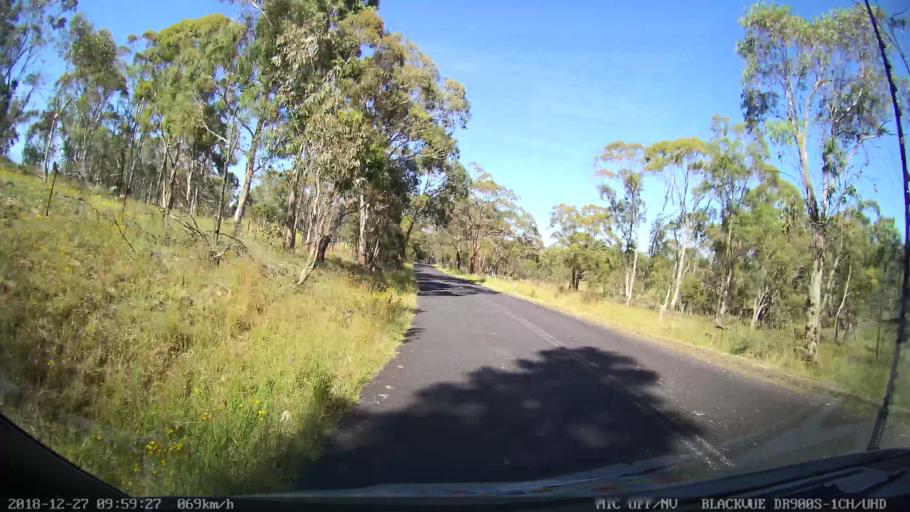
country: AU
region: New South Wales
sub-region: Lithgow
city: Portland
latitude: -33.4338
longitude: 149.9517
